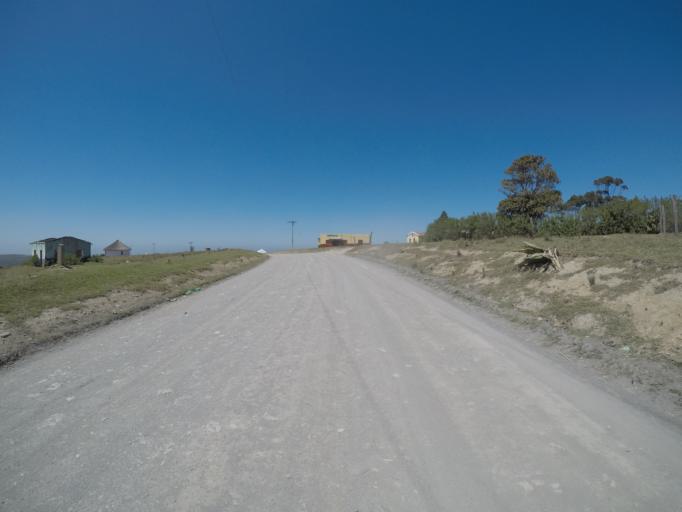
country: ZA
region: Eastern Cape
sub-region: OR Tambo District Municipality
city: Libode
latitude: -31.9829
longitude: 29.0365
